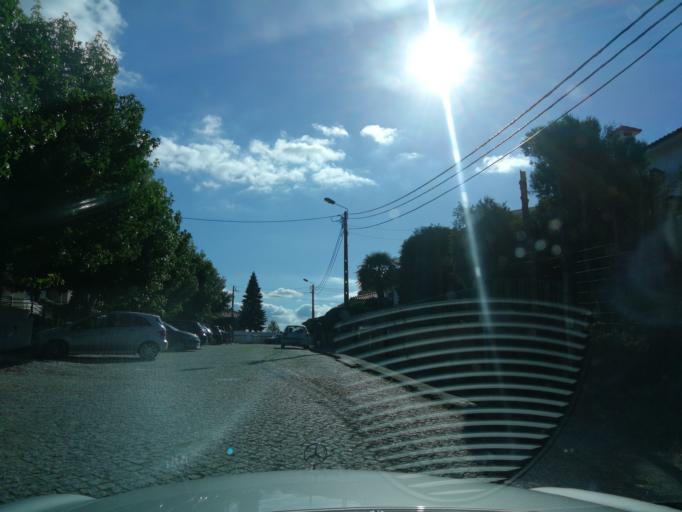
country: PT
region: Braga
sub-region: Braga
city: Adaufe
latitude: 41.5726
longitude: -8.3803
